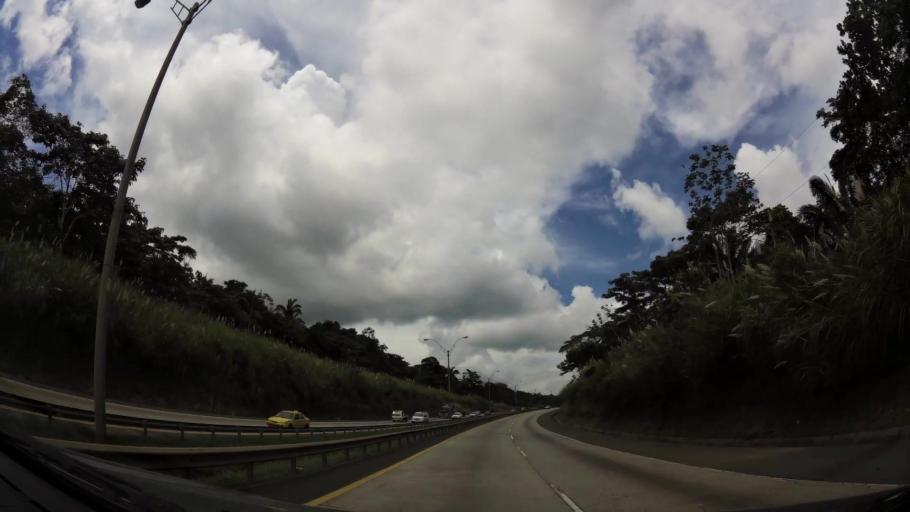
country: PA
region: Panama
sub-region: Distrito Arraijan
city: Arraijan
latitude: 8.9825
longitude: -79.6479
